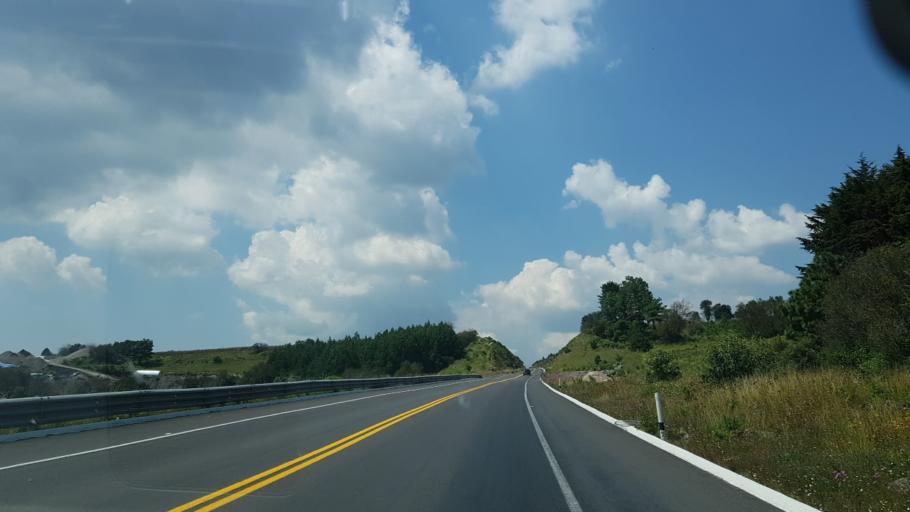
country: MX
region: Mexico
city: Amanalco de Becerra
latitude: 19.3556
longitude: -99.9696
